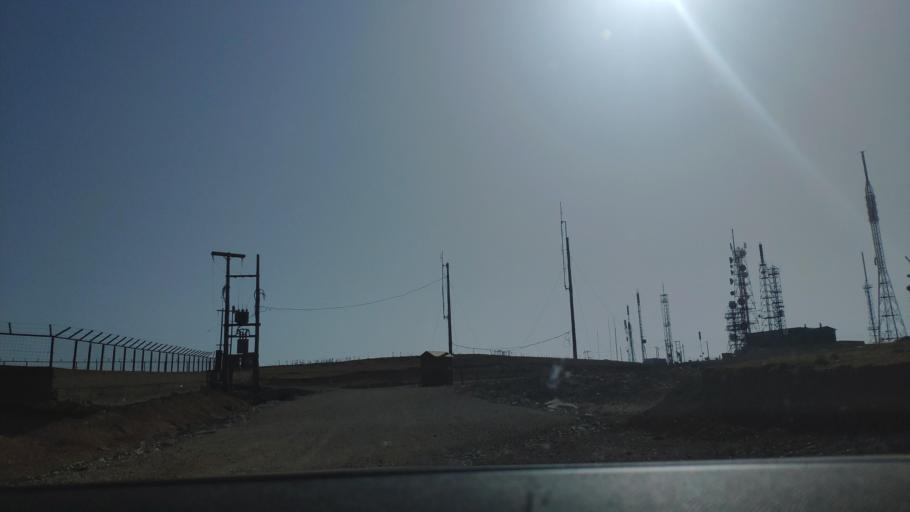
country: GR
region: West Greece
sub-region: Nomos Aitolias kai Akarnanias
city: Monastirakion
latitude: 38.8081
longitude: 20.9815
